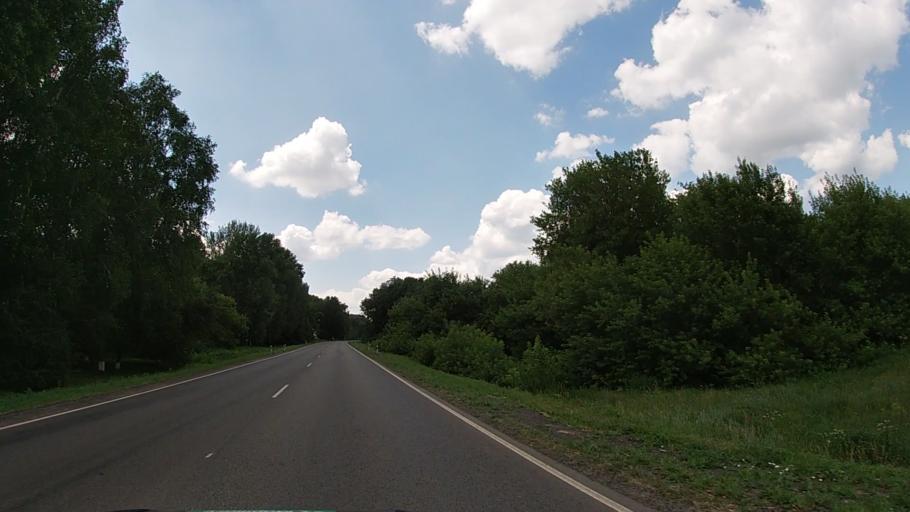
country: RU
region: Belgorod
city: Grayvoron
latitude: 50.4964
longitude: 35.7140
